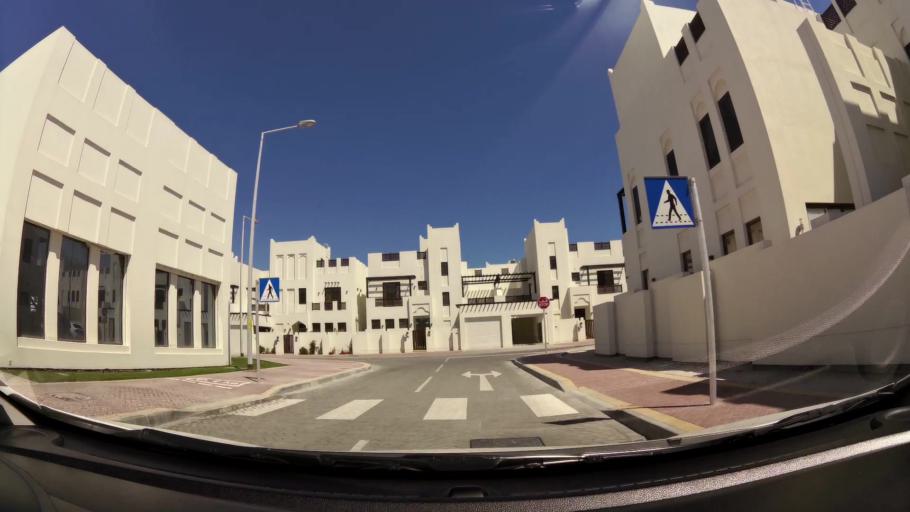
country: BH
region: Muharraq
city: Al Muharraq
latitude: 26.3017
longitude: 50.6387
